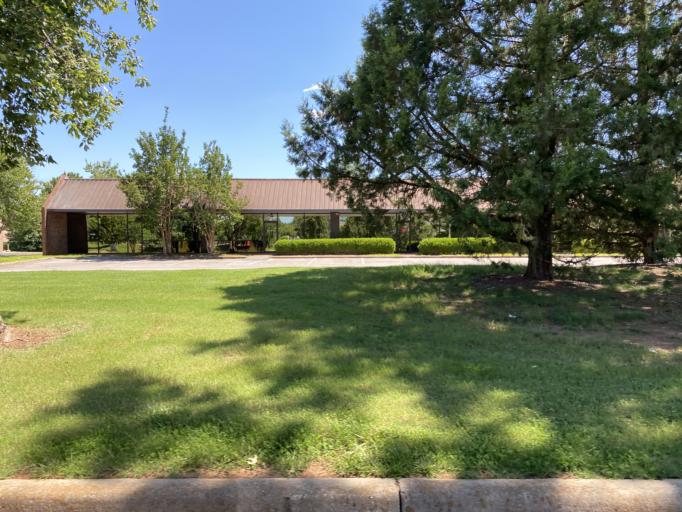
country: US
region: Alabama
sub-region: Madison County
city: Redstone Arsenal
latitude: 34.7411
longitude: -86.6548
